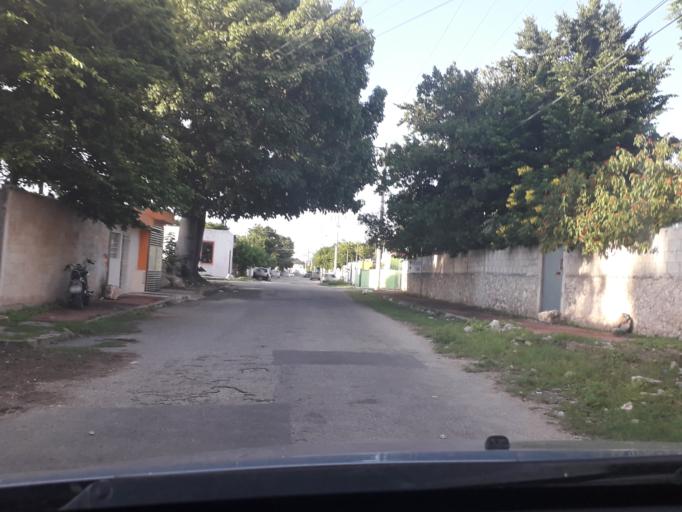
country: MX
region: Yucatan
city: Merida
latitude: 20.9788
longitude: -89.6514
